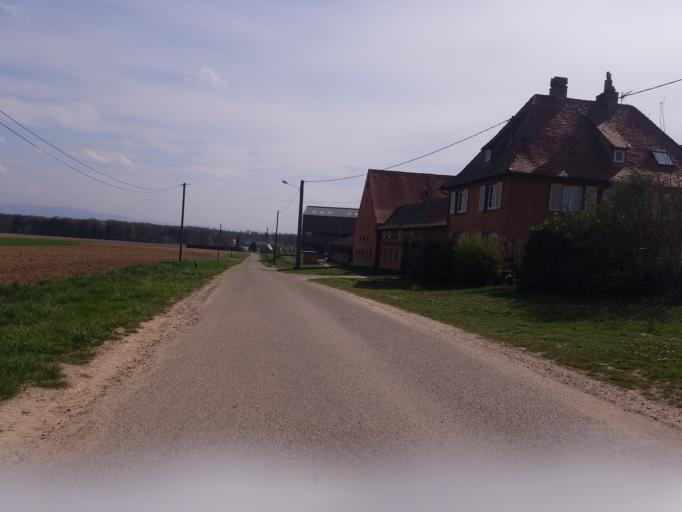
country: FR
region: Alsace
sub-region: Departement du Bas-Rhin
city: Betschdorf
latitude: 48.8994
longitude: 7.9531
